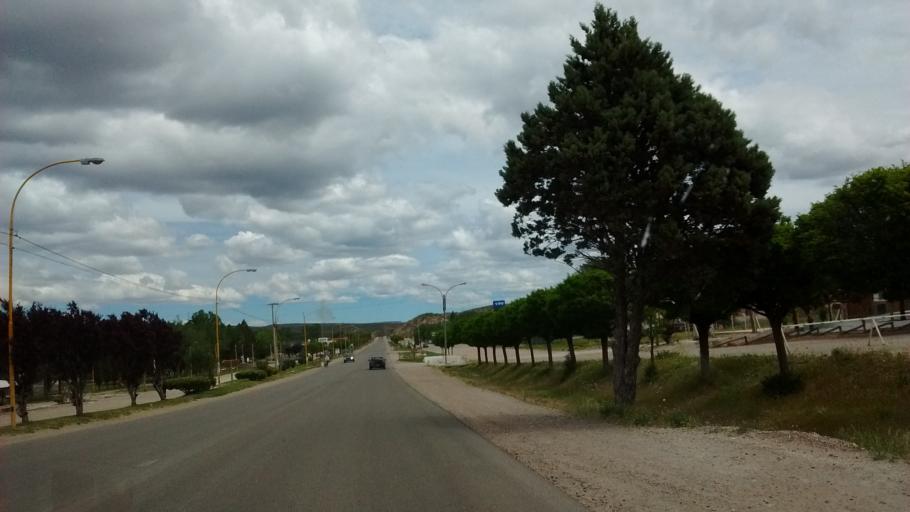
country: AR
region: Neuquen
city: Piedra del Aguila
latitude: -40.0468
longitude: -70.0745
